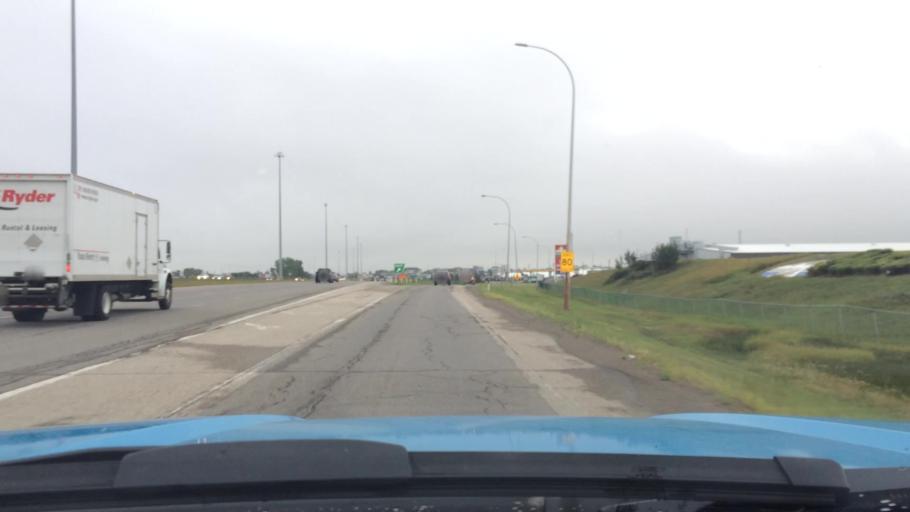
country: CA
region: Alberta
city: Airdrie
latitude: 51.2833
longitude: -114.0010
